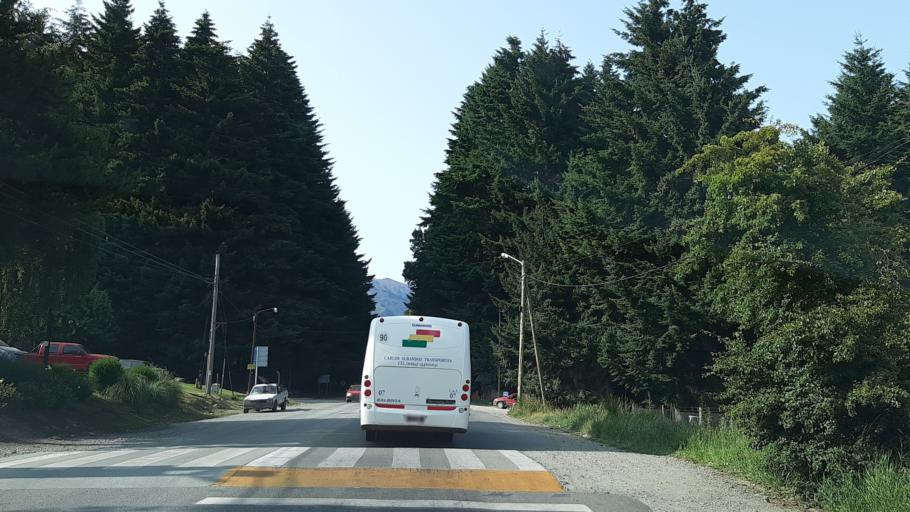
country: AR
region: Rio Negro
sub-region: Departamento de Bariloche
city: San Carlos de Bariloche
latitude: -41.1590
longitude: -71.4080
